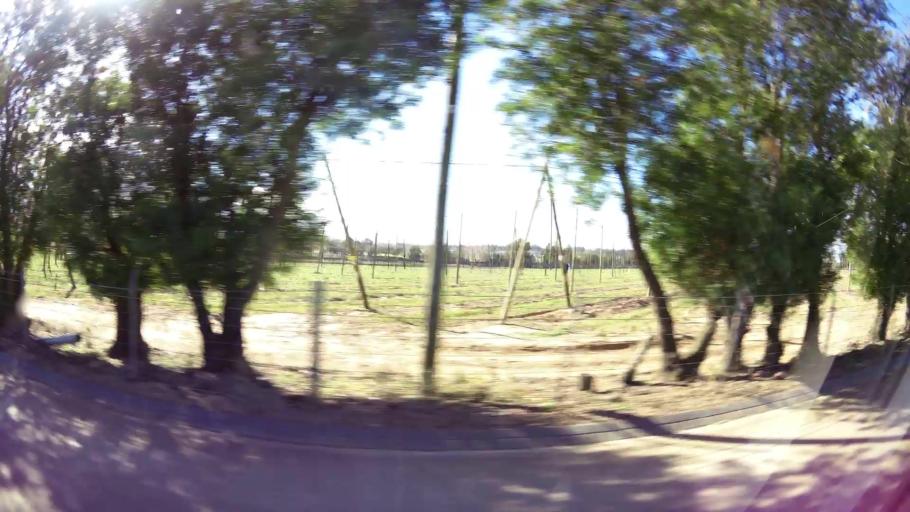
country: ZA
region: Western Cape
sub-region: Eden District Municipality
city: George
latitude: -33.9599
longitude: 22.3990
